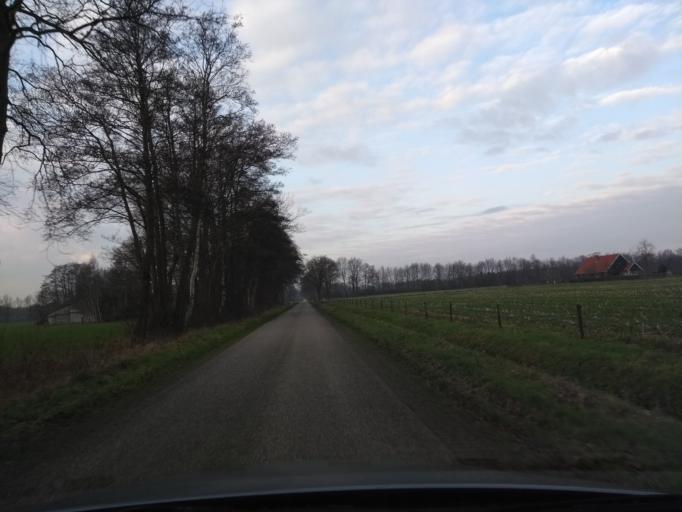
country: NL
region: Overijssel
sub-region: Gemeente Haaksbergen
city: Haaksbergen
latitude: 52.1344
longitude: 6.7535
